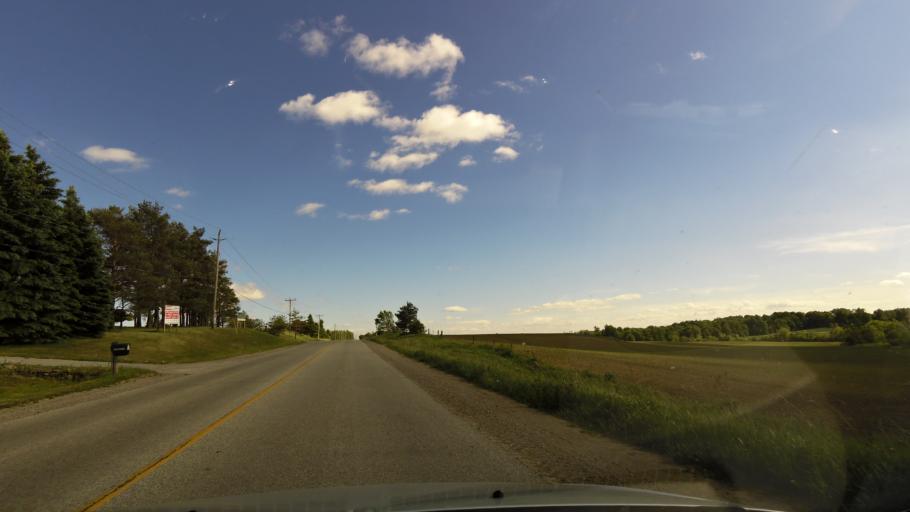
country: CA
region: Ontario
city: Bradford West Gwillimbury
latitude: 44.1406
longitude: -79.6105
